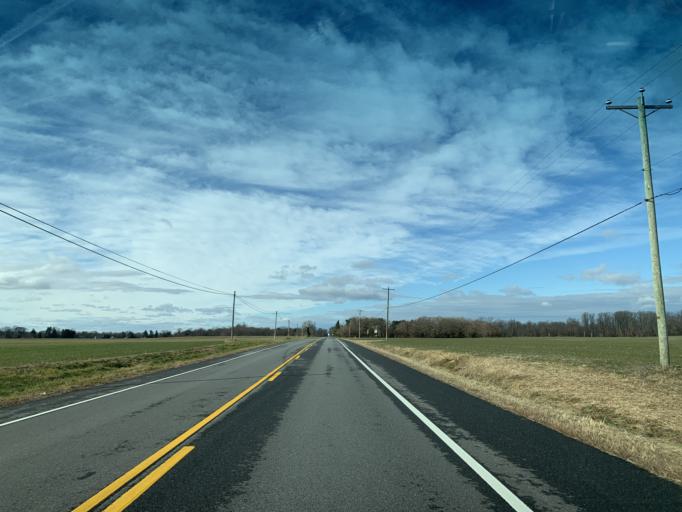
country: US
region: Maryland
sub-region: Kent County
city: Chestertown
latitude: 39.3250
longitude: -76.0308
